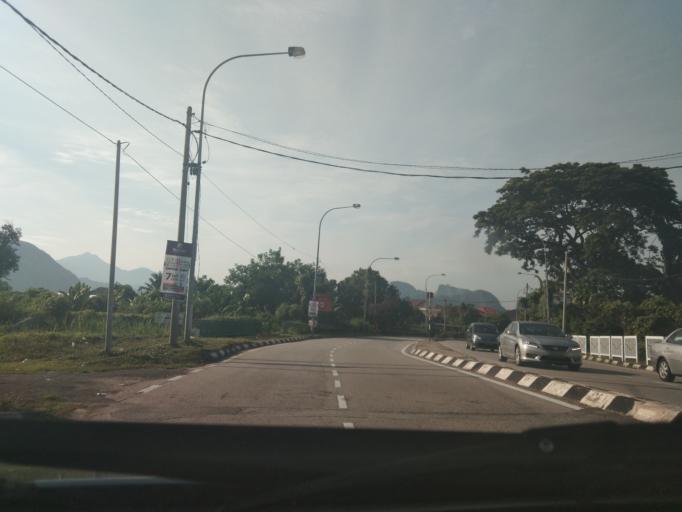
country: MY
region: Perak
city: Ipoh
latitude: 4.5886
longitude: 101.1269
